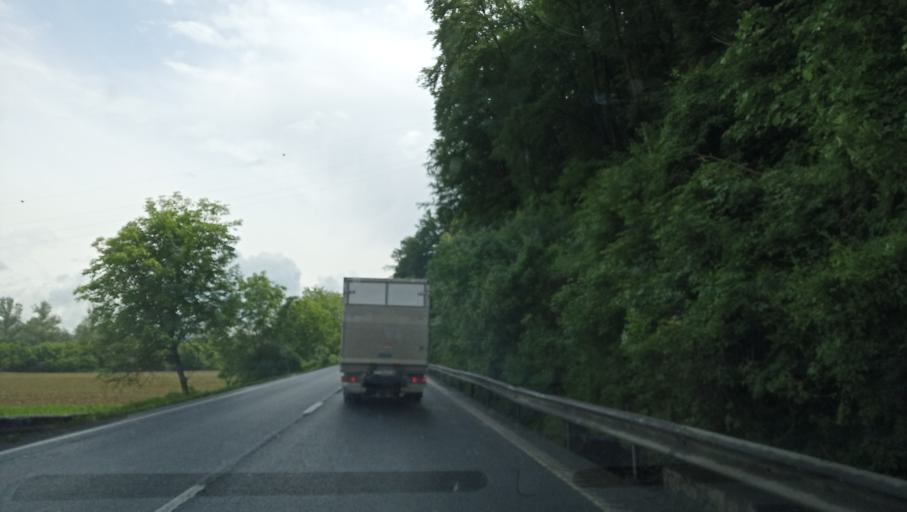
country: RO
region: Hunedoara
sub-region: Comuna Ilia
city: Ilia
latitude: 45.9233
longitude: 22.6793
